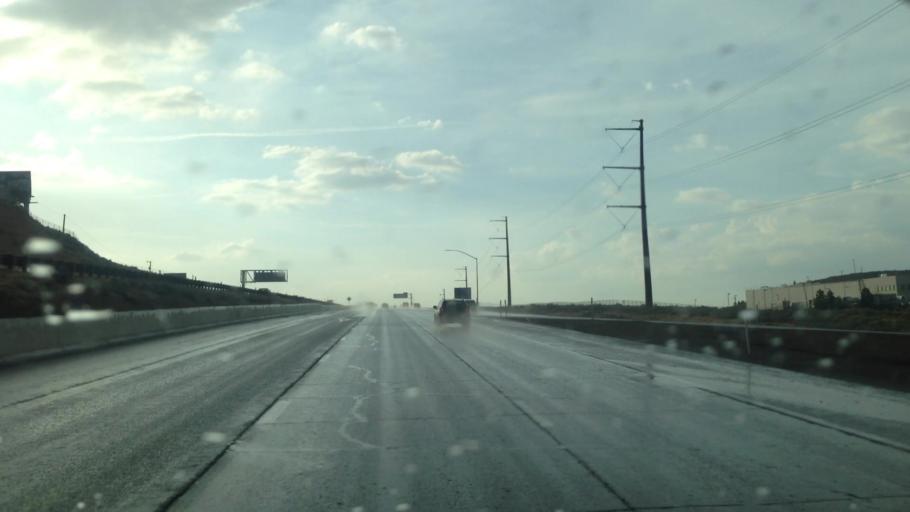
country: US
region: Nevada
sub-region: Washoe County
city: Golden Valley
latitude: 39.5921
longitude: -119.8286
